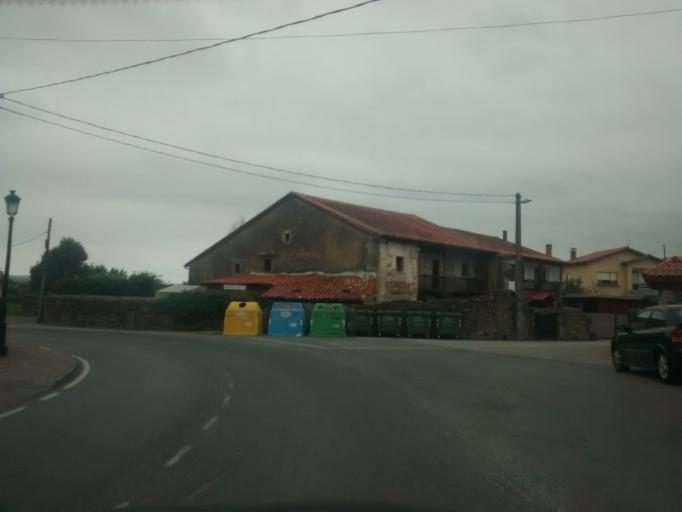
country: ES
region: Cantabria
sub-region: Provincia de Cantabria
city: Luzmela
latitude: 43.2979
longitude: -4.2092
